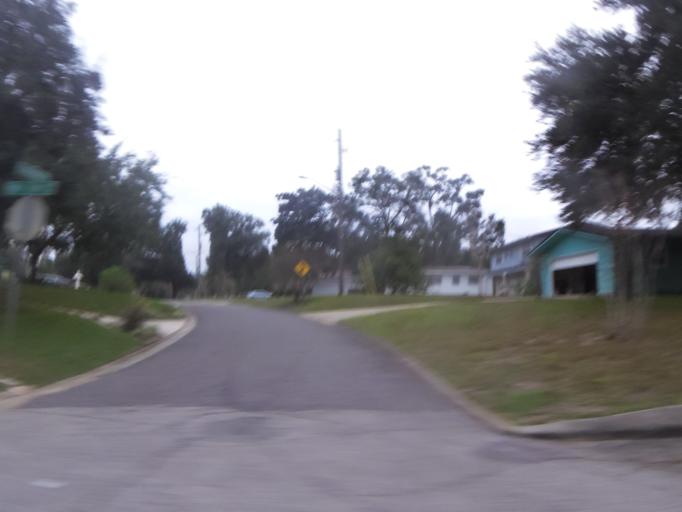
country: US
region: Florida
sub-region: Clay County
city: Bellair-Meadowbrook Terrace
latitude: 30.2730
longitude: -81.7408
